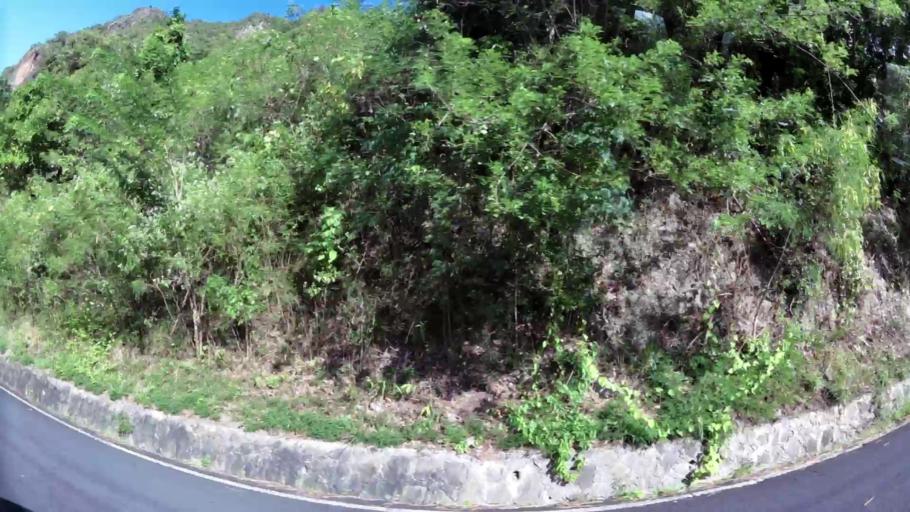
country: LC
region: Soufriere
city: Soufriere
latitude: 13.8604
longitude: -61.0554
